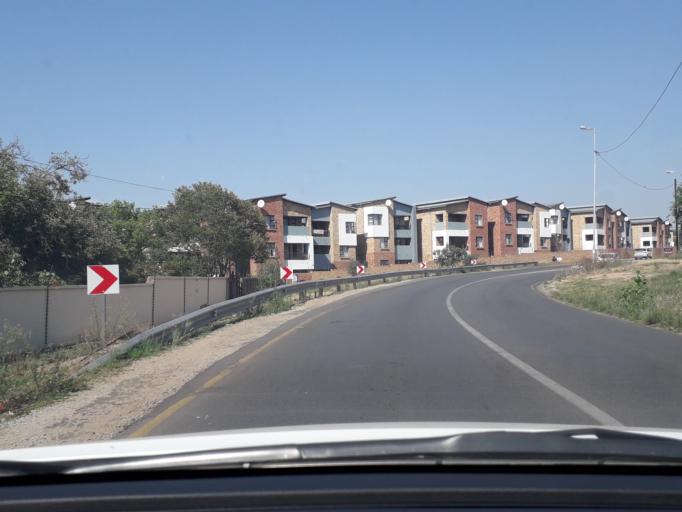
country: ZA
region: Gauteng
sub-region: City of Johannesburg Metropolitan Municipality
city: Roodepoort
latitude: -26.0857
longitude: 27.9396
